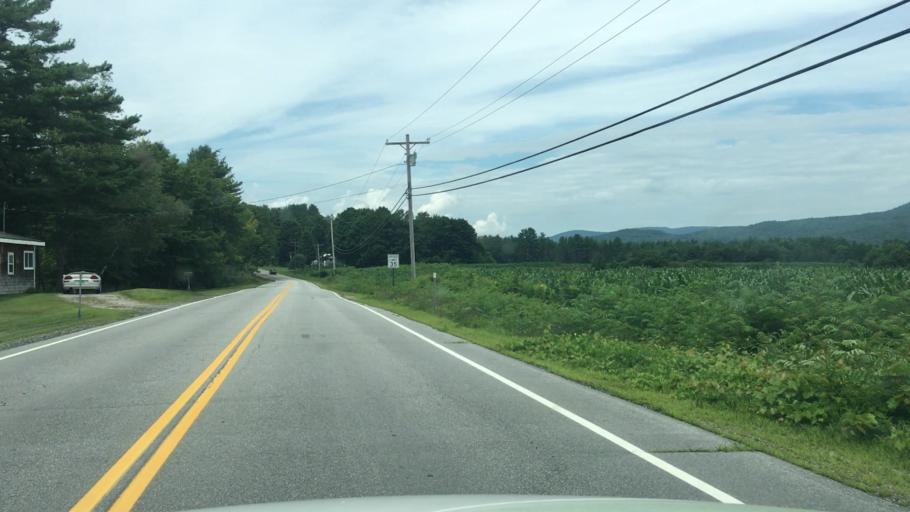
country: US
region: New Hampshire
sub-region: Grafton County
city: Plymouth
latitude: 43.7778
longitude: -71.7439
